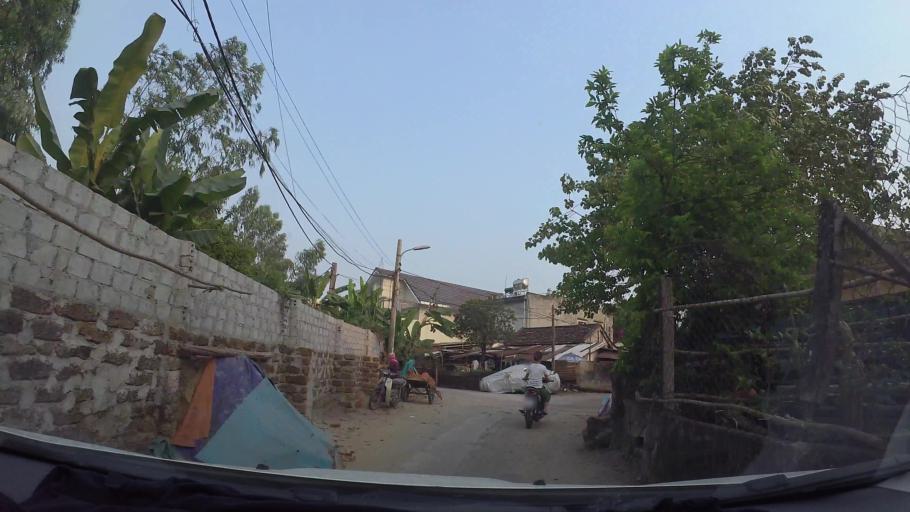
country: VN
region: Da Nang
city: Cam Le
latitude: 16.0213
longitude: 108.1950
